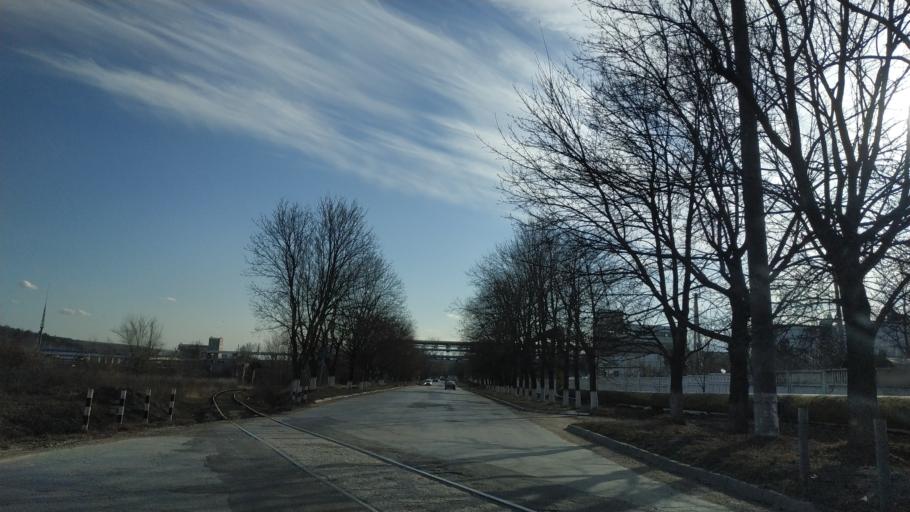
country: MD
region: Chisinau
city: Chisinau
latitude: 47.0303
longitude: 28.8965
